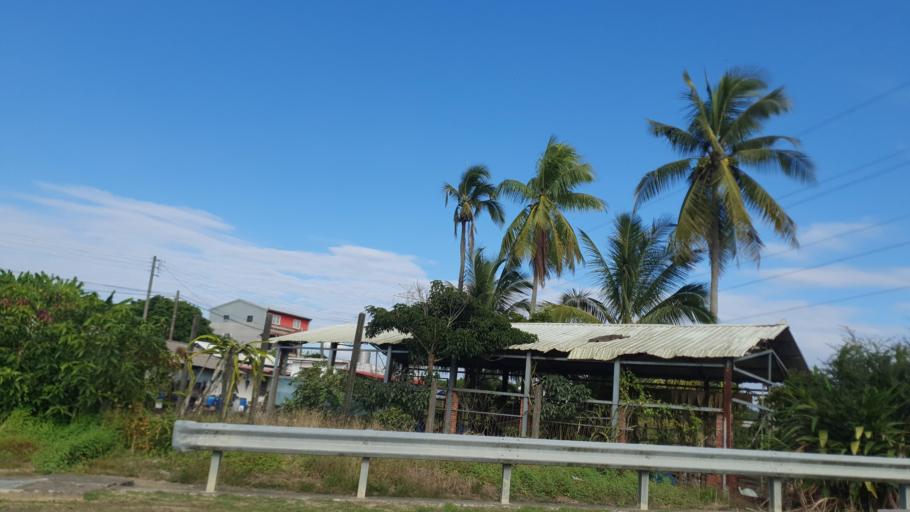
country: TW
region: Taiwan
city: Yujing
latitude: 23.0494
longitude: 120.4217
